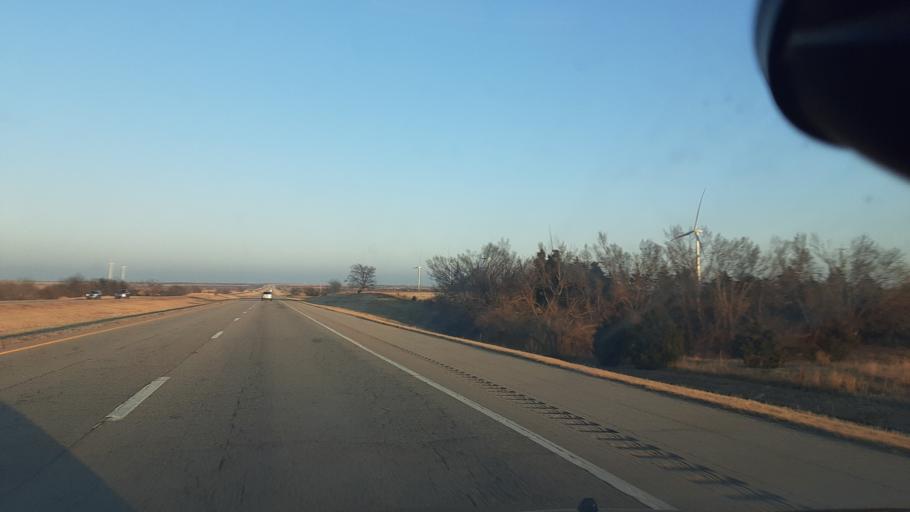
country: US
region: Oklahoma
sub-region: Noble County
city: Perry
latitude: 36.3978
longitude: -97.4312
